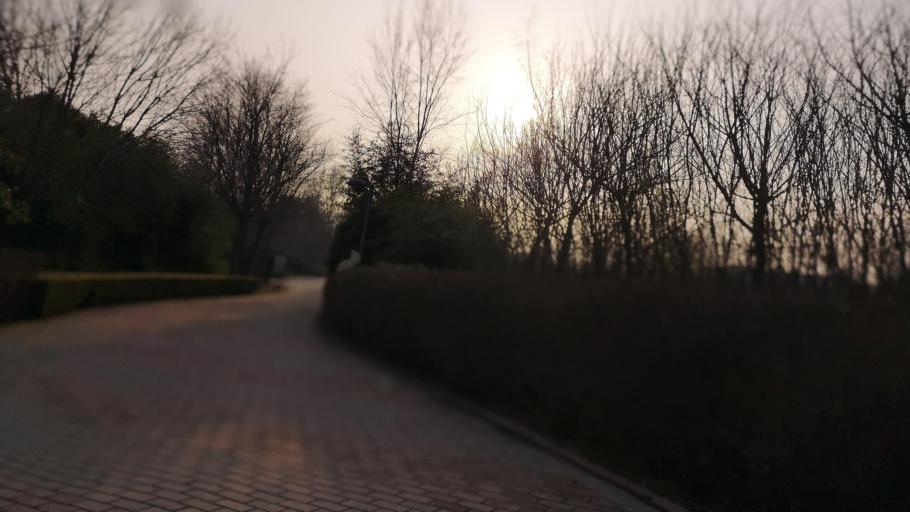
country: CN
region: Henan Sheng
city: Zhongyuanlu
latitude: 35.7450
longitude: 115.0635
